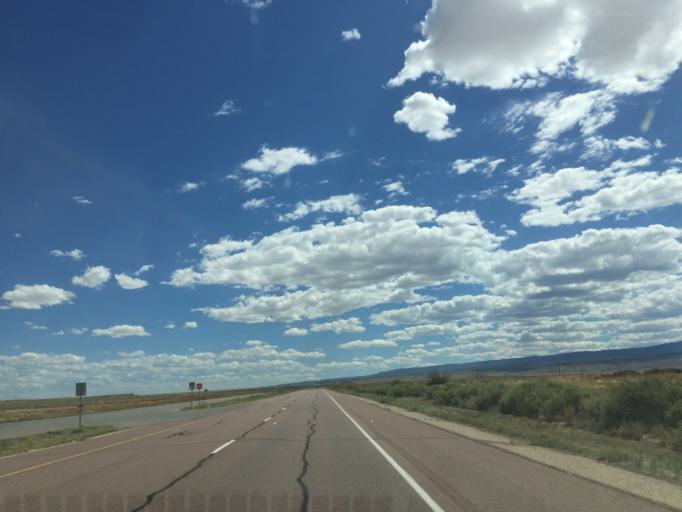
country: US
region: New Mexico
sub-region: McKinley County
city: Navajo
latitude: 36.2508
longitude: -108.7074
